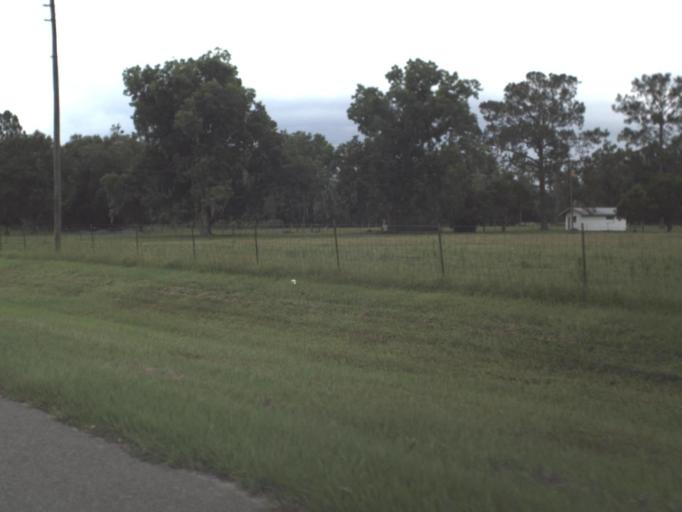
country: US
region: Florida
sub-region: Clay County
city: Keystone Heights
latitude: 29.8594
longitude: -82.0729
